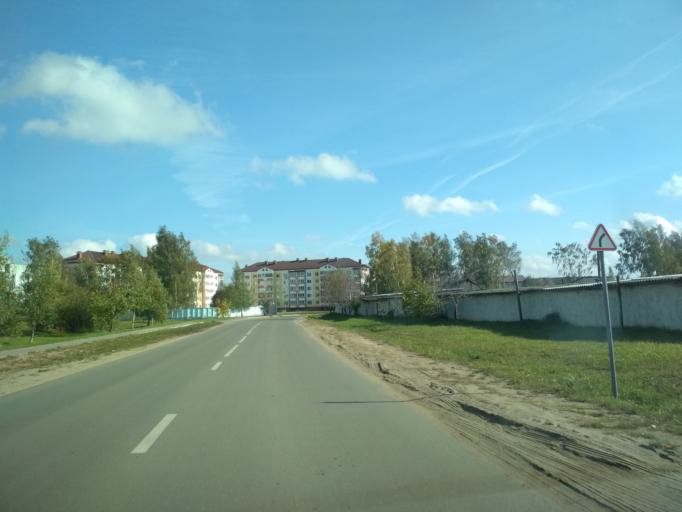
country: BY
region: Minsk
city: Mar''ina Horka
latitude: 53.5021
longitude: 28.1598
